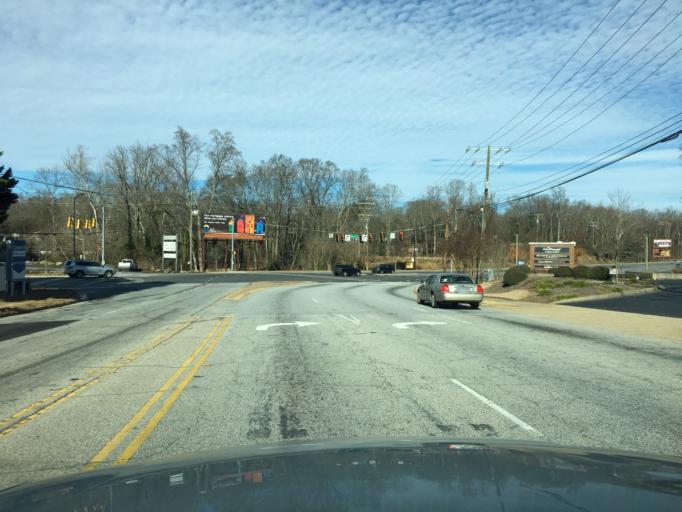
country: US
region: South Carolina
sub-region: Greenville County
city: Greenville
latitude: 34.8616
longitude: -82.3849
